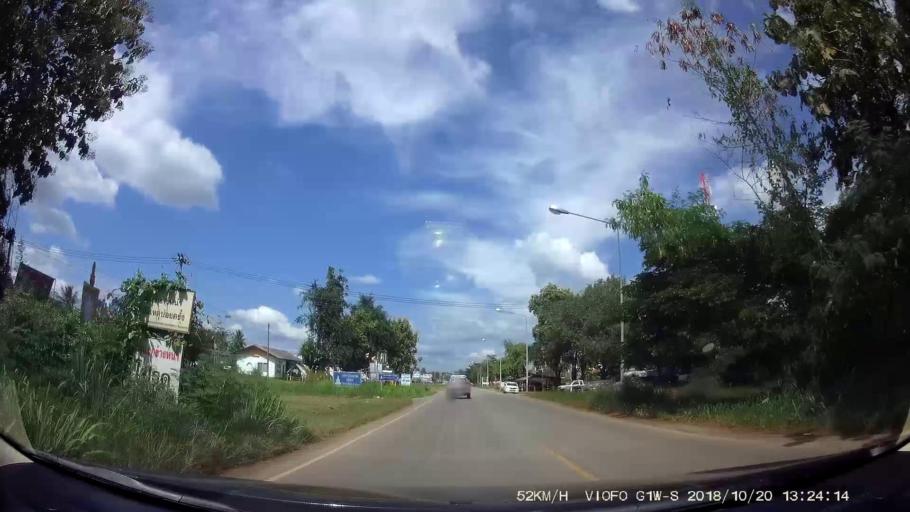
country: TH
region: Chaiyaphum
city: Khon San
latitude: 16.5916
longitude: 101.9255
